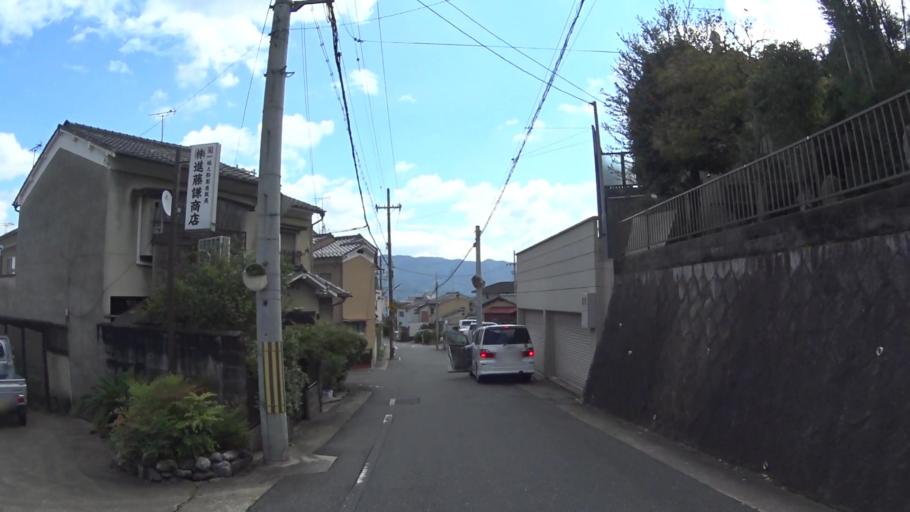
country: JP
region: Kyoto
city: Kyoto
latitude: 34.9731
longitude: 135.7942
